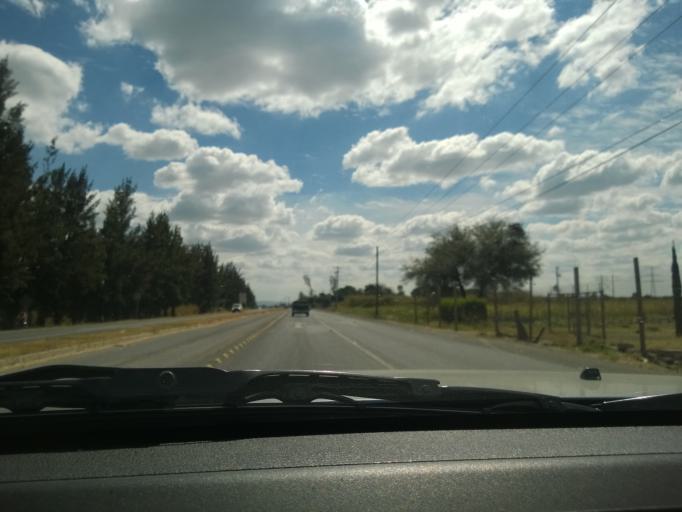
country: MX
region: Guanajuato
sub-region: Leon
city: El CERESO
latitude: 21.0218
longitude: -101.6981
